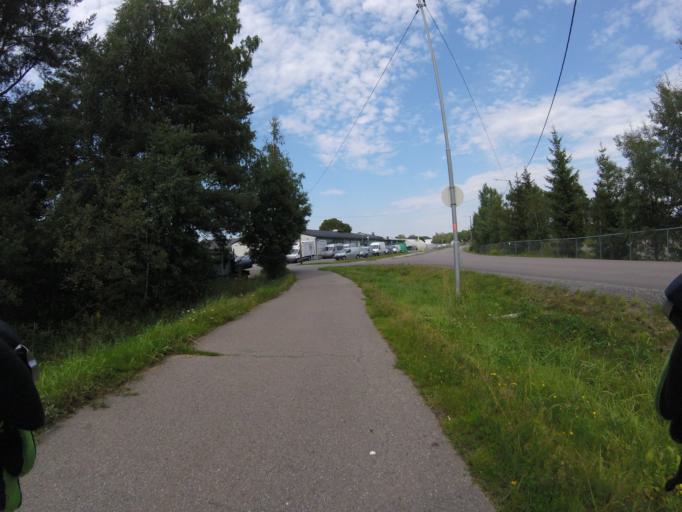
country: NO
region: Akershus
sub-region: Skedsmo
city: Lillestrom
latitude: 59.9516
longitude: 11.0749
